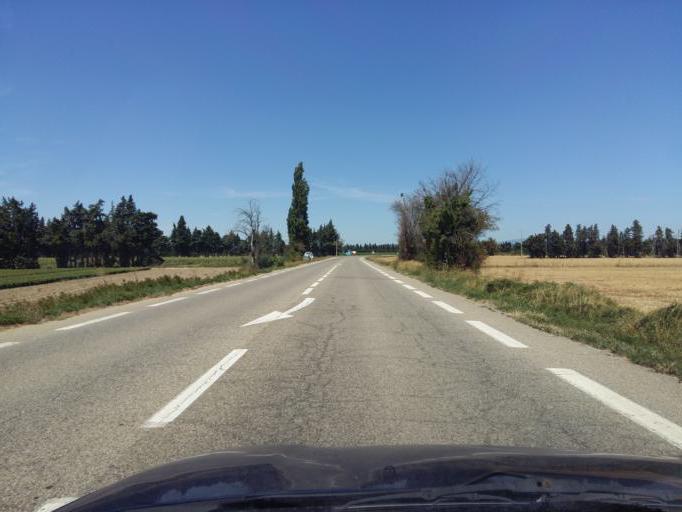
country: FR
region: Provence-Alpes-Cote d'Azur
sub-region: Departement du Vaucluse
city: Jonquieres
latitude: 44.1289
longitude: 4.9340
